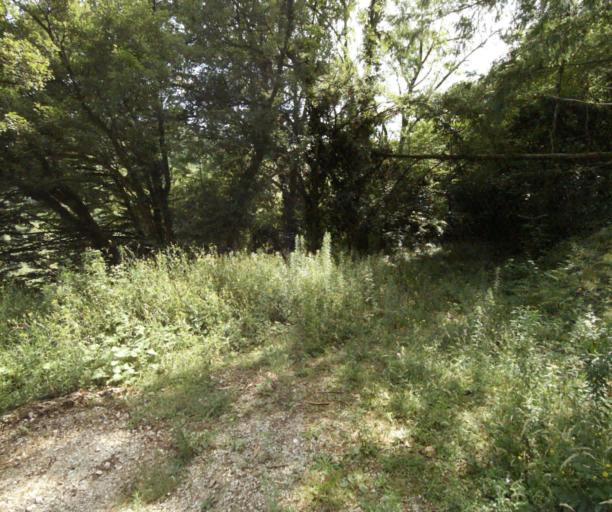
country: FR
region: Midi-Pyrenees
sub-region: Departement du Tarn
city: Soreze
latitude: 43.4535
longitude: 2.1065
